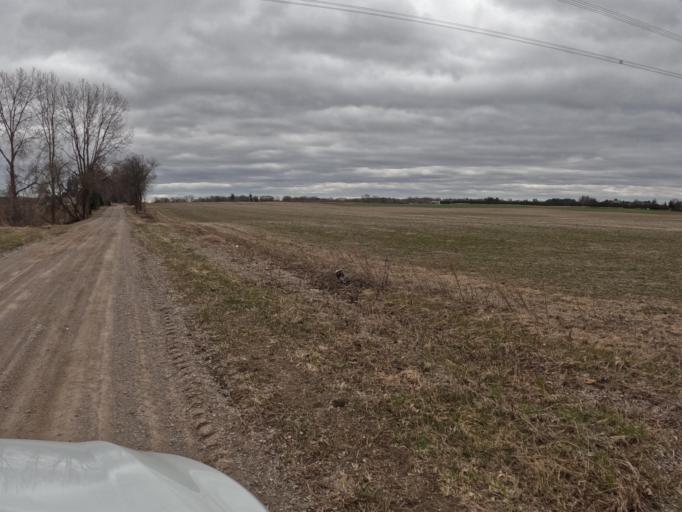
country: CA
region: Ontario
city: Norfolk County
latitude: 42.9668
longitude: -80.3910
